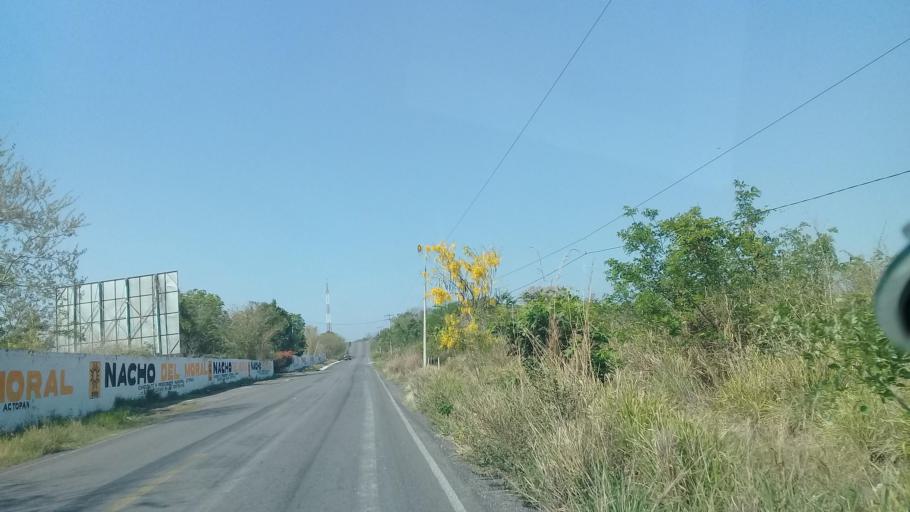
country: MX
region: Veracruz
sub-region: Emiliano Zapata
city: Plan del Rio
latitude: 19.3996
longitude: -96.6160
